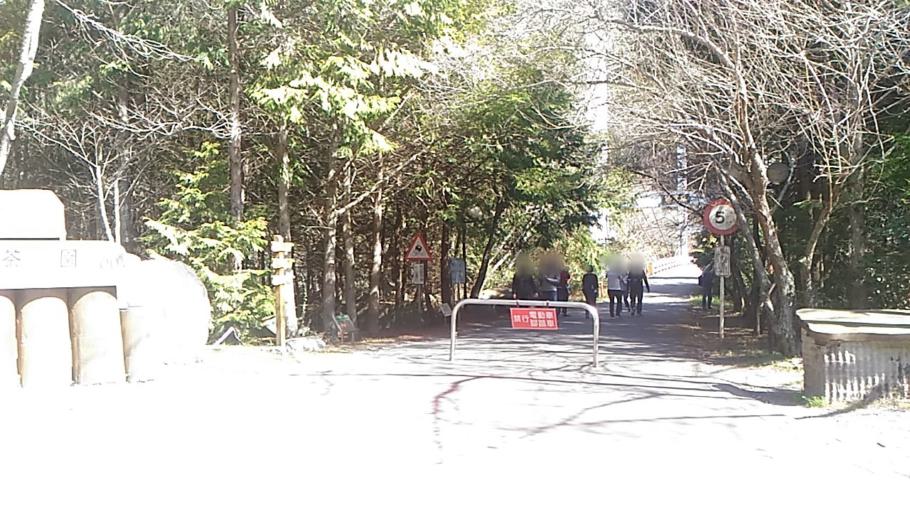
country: TW
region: Taiwan
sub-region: Hualien
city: Hualian
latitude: 24.3572
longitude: 121.3122
